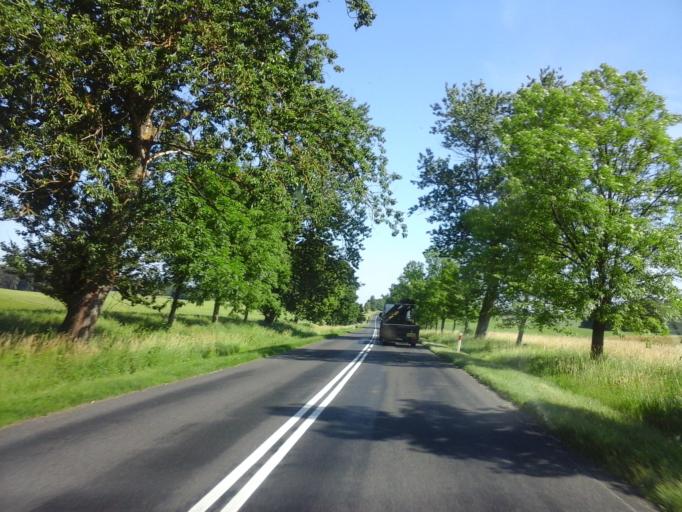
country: PL
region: West Pomeranian Voivodeship
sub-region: Powiat swidwinski
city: Polczyn-Zdroj
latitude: 53.8072
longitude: 16.0751
